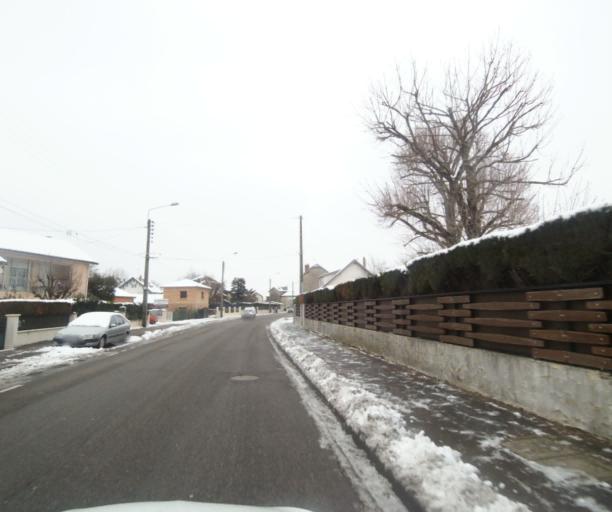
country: FR
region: Champagne-Ardenne
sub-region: Departement de la Haute-Marne
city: Saint-Dizier
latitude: 48.6334
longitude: 4.9362
